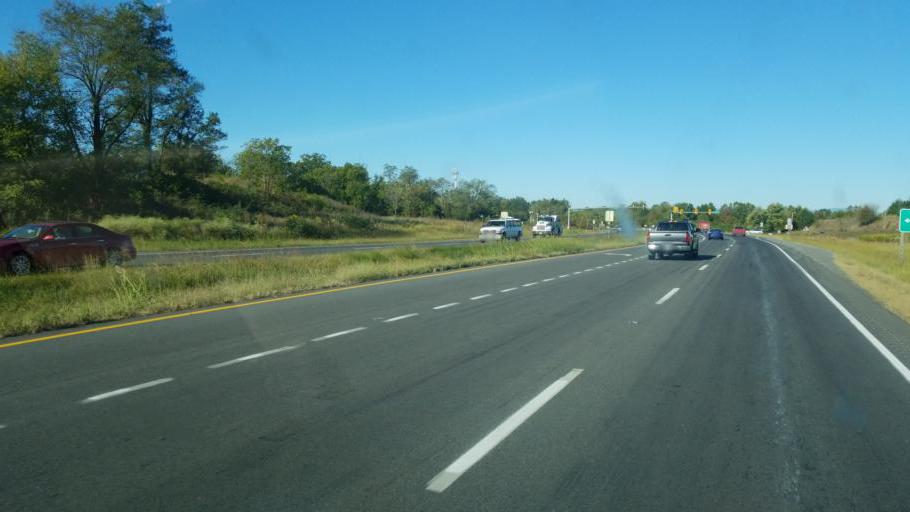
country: US
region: Virginia
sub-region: Culpeper County
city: Culpeper
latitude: 38.5036
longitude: -77.8921
